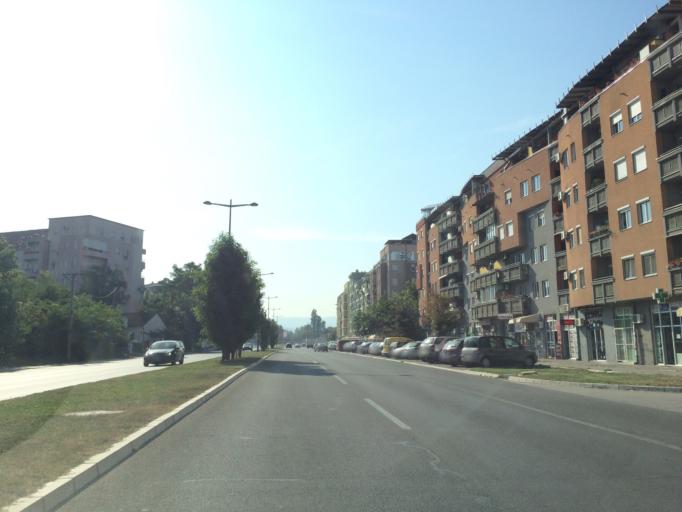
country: RS
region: Autonomna Pokrajina Vojvodina
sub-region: Juznobacki Okrug
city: Novi Sad
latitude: 45.2428
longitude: 19.8204
